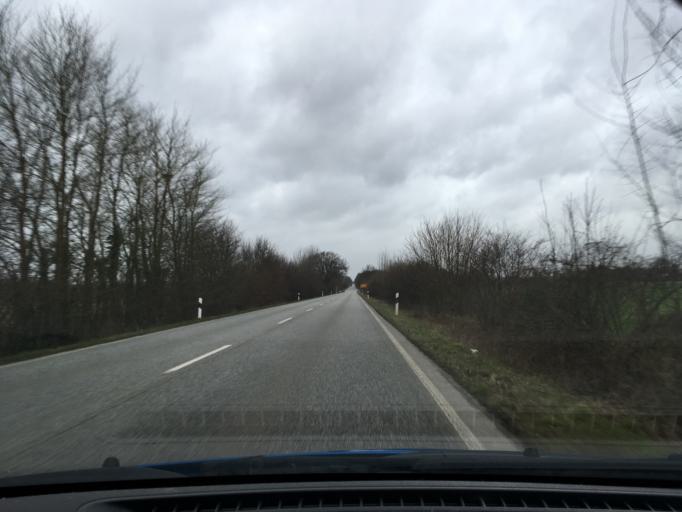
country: DE
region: Schleswig-Holstein
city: Wangelau
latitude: 53.4503
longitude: 10.5549
